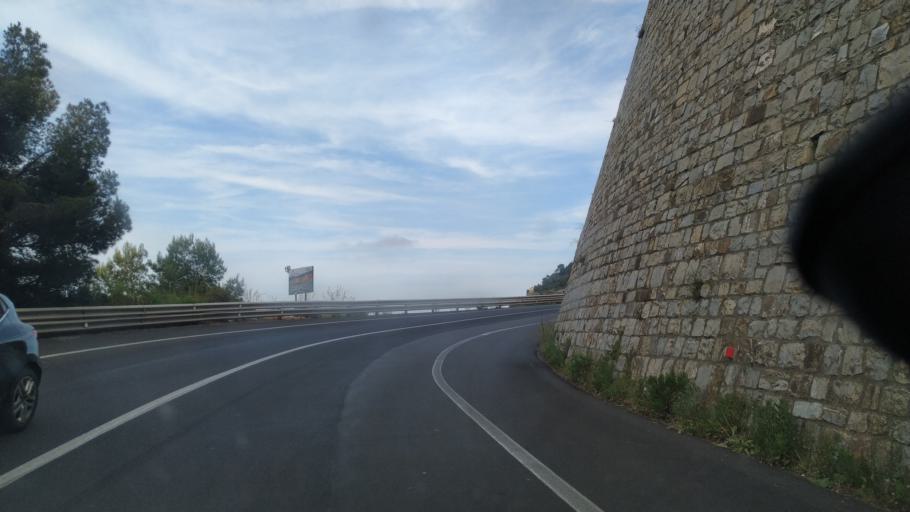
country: IT
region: Liguria
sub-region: Provincia di Savona
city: Laigueglia
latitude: 43.9657
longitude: 8.1654
